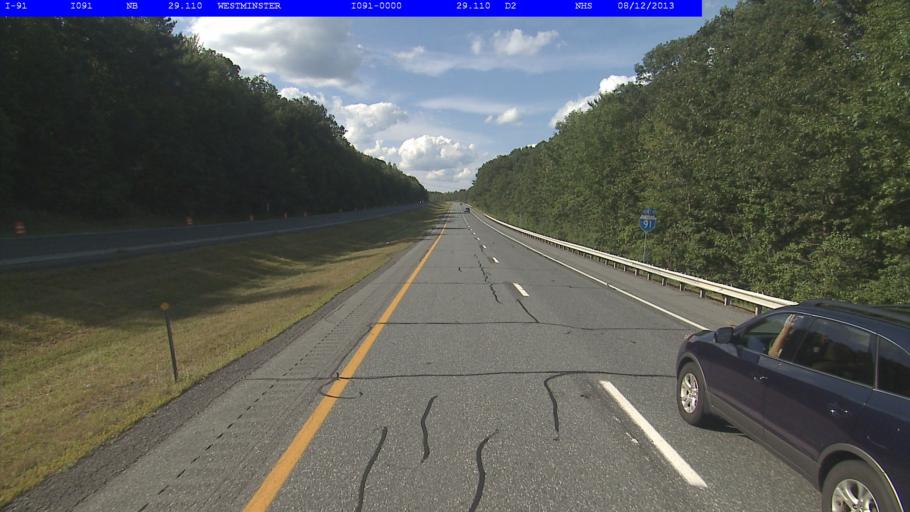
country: US
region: Vermont
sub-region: Windham County
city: Bellows Falls
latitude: 43.0985
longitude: -72.4540
